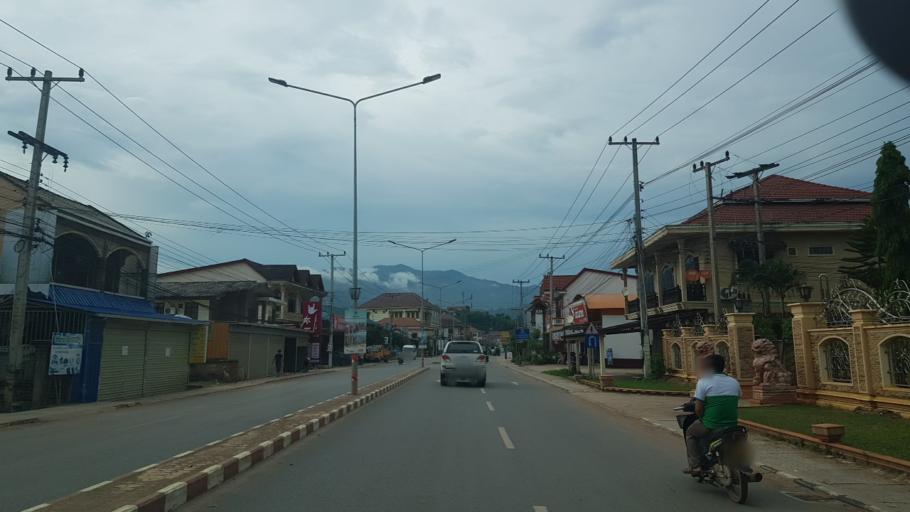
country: LA
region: Oudomxai
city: Muang Xay
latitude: 20.6815
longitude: 101.9865
